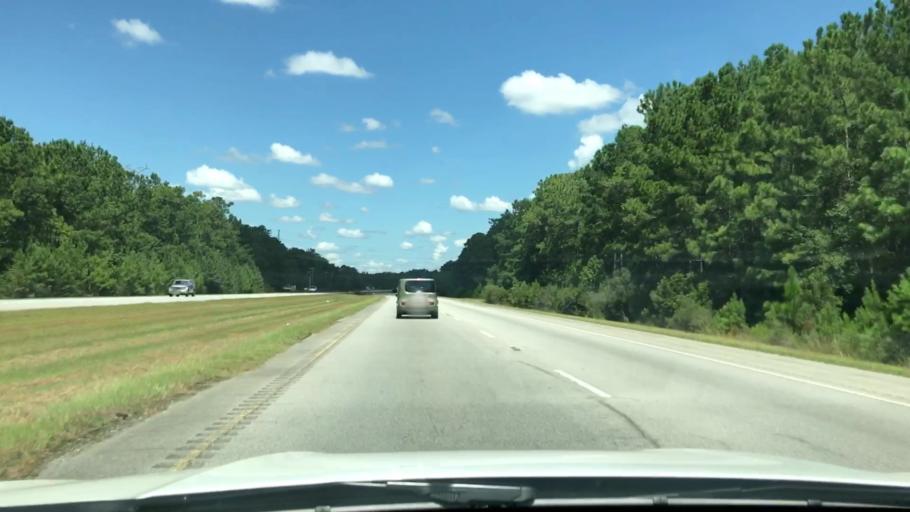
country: US
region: South Carolina
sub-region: Berkeley County
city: Hanahan
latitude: 32.9530
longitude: -80.0015
